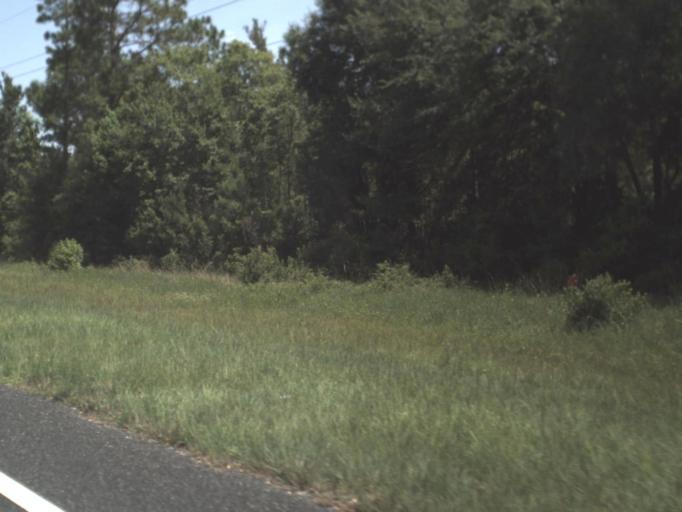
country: US
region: Florida
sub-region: Taylor County
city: Steinhatchee
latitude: 29.6987
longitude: -83.2818
